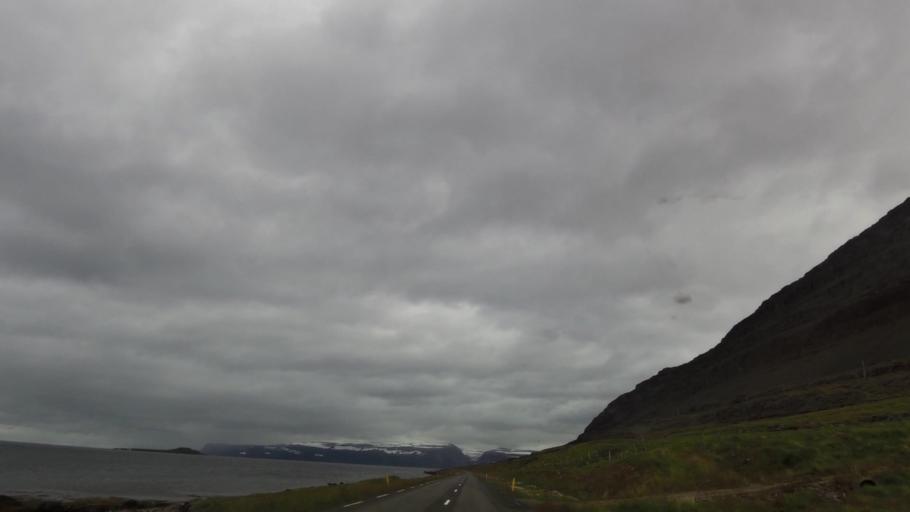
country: IS
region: Westfjords
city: Isafjoerdur
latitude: 66.0101
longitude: -22.7824
